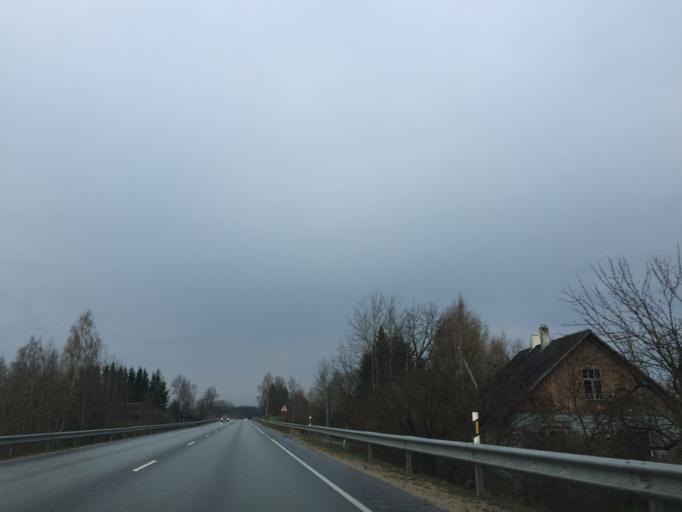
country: EE
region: Tartu
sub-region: UElenurme vald
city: Ulenurme
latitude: 58.1844
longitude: 26.6932
